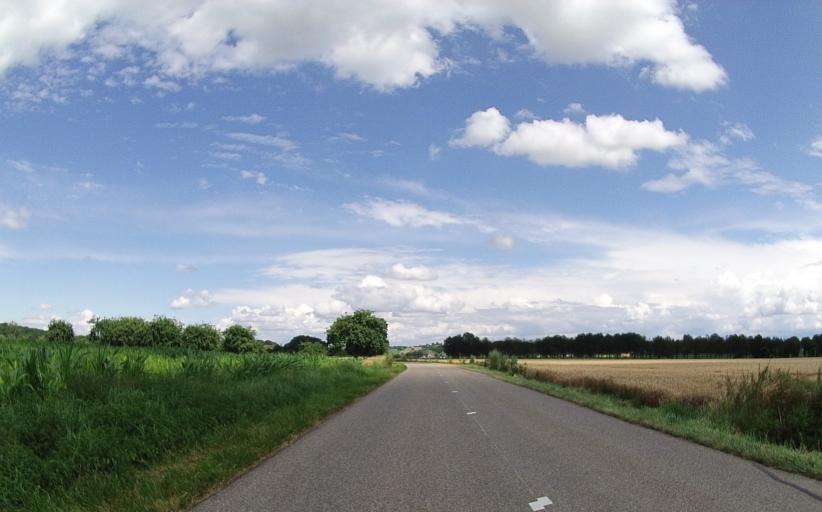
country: FR
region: Alsace
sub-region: Departement du Bas-Rhin
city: Surbourg
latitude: 48.9156
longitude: 7.8129
